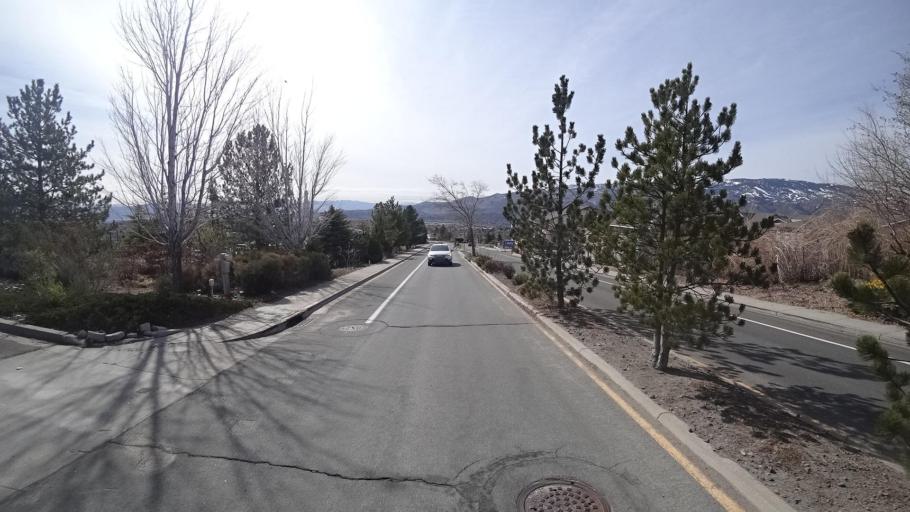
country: US
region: Nevada
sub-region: Washoe County
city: Mogul
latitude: 39.5345
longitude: -119.9010
